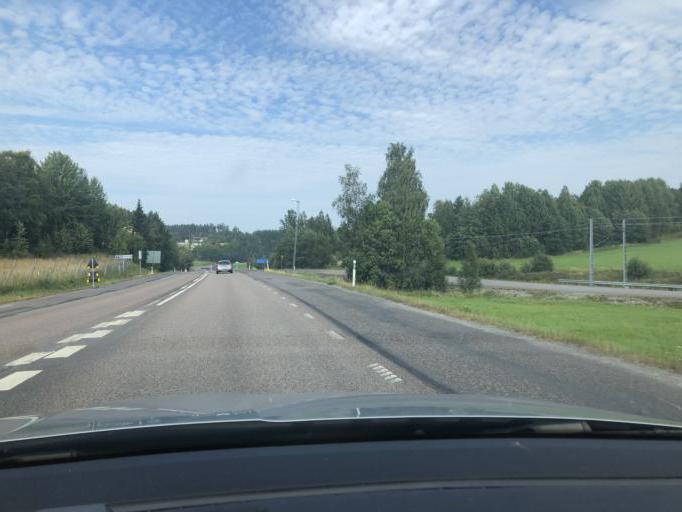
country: SE
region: Vaesternorrland
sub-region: Kramfors Kommun
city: Kramfors
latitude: 62.8764
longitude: 17.8556
